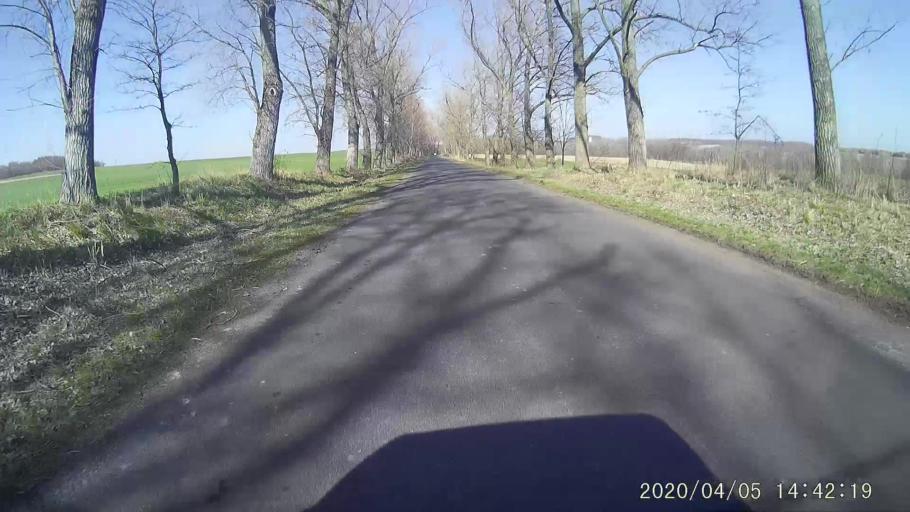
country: PL
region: Lower Silesian Voivodeship
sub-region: Powiat lubanski
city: Siekierczyn
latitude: 51.0550
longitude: 15.1481
